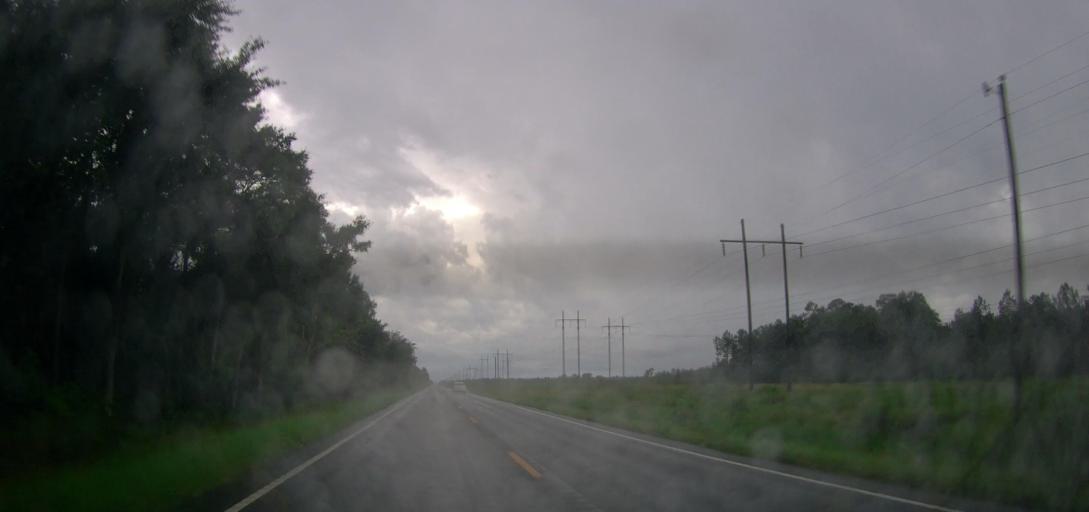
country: US
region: Georgia
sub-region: Brantley County
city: Nahunta
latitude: 31.3392
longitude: -81.8495
